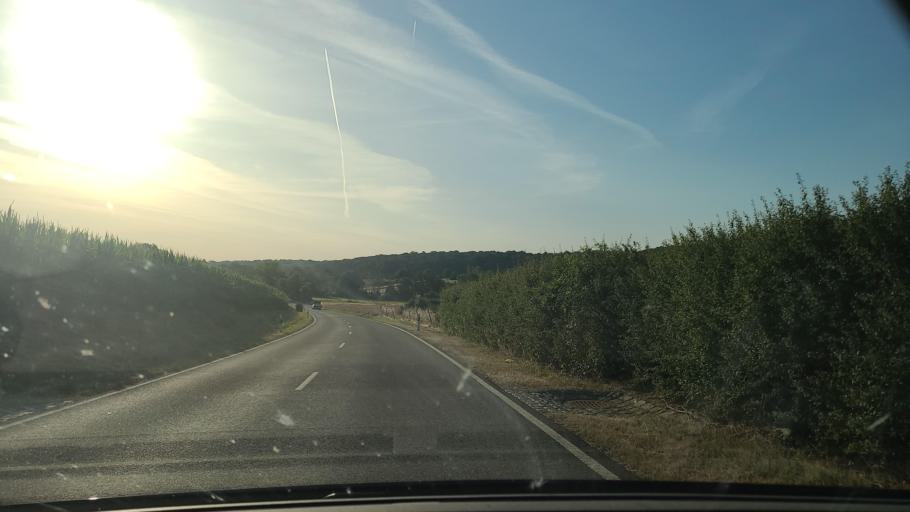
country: LU
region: Luxembourg
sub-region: Canton de Capellen
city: Dippach
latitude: 49.6127
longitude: 5.9811
